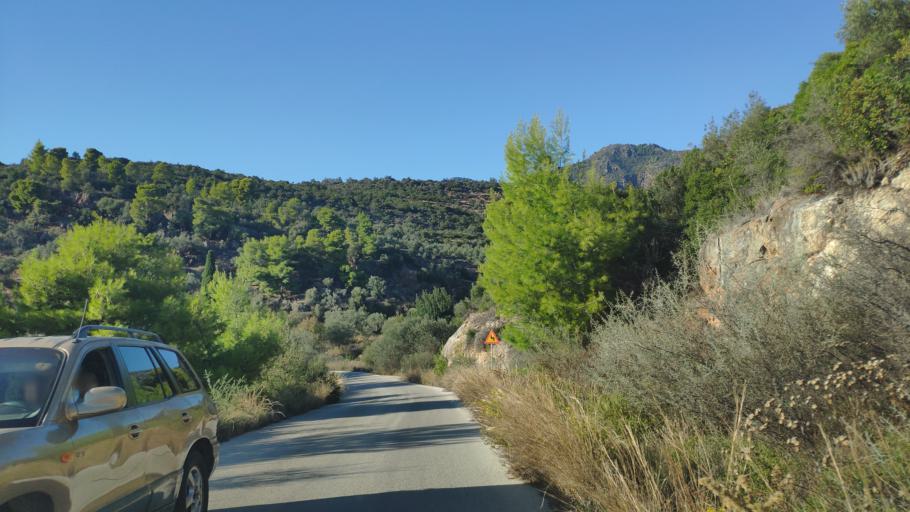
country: GR
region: Attica
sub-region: Nomos Piraios
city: Galatas
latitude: 37.5780
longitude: 23.3583
